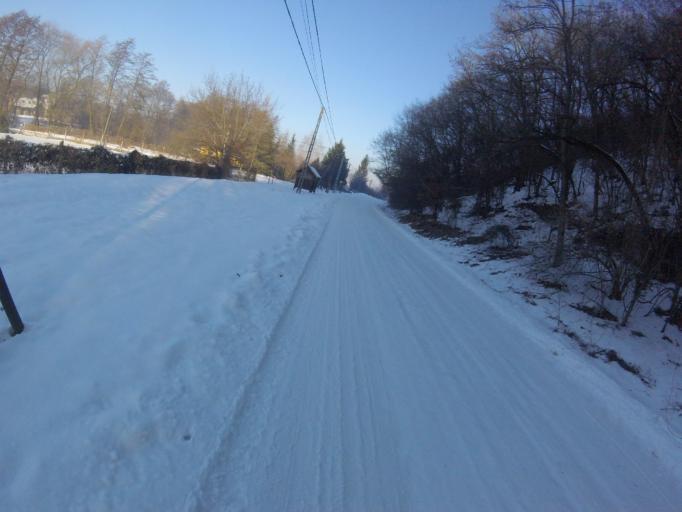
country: SK
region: Nitriansky
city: Sahy
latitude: 48.0083
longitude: 18.8918
